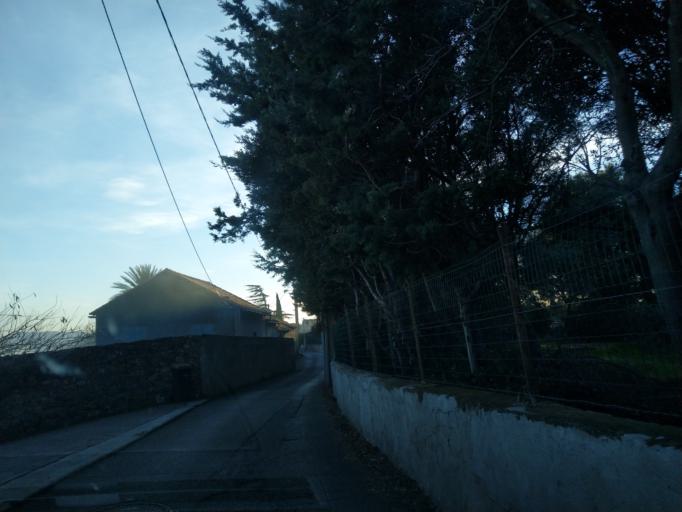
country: FR
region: Provence-Alpes-Cote d'Azur
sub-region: Departement des Bouches-du-Rhone
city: Plan-de-Cuques
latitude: 43.3554
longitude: 5.4603
